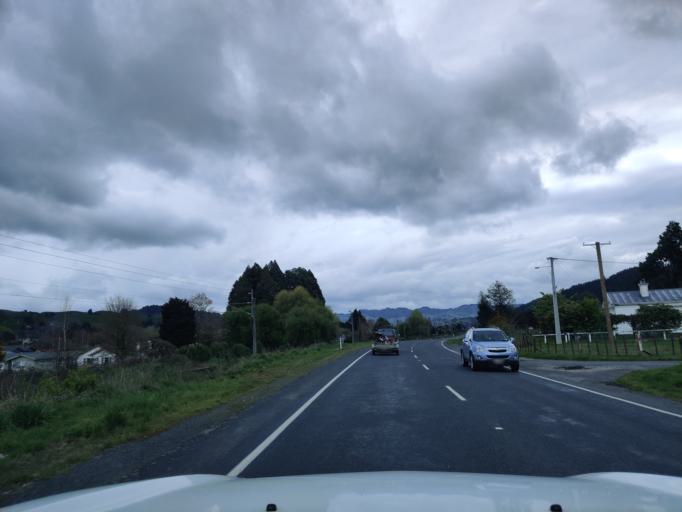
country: NZ
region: Waikato
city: Turangi
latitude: -38.8811
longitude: 175.2984
